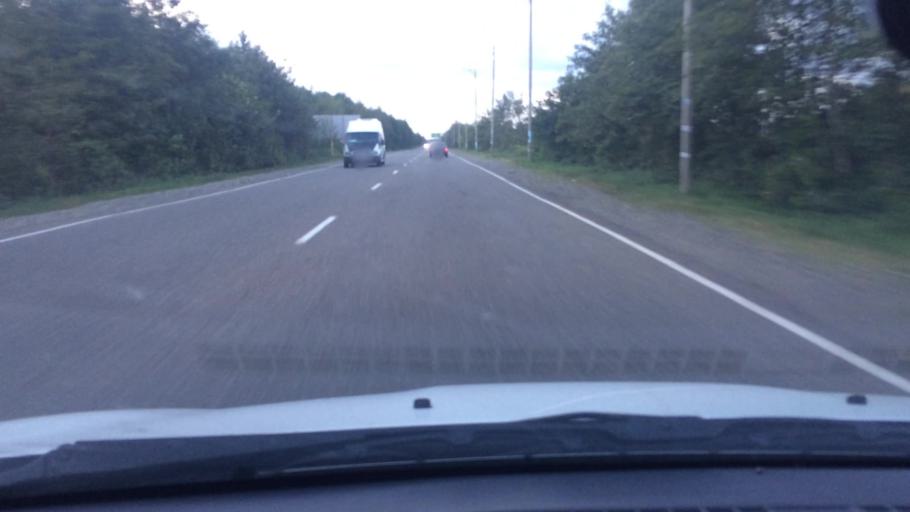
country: GE
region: Guria
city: Urek'i
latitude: 41.9290
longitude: 41.7728
